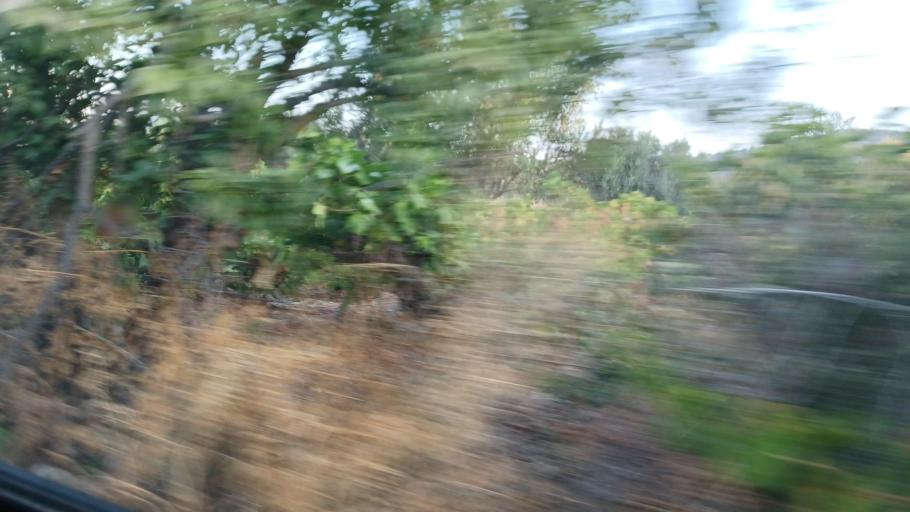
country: CY
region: Pafos
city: Tala
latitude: 34.9172
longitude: 32.4893
